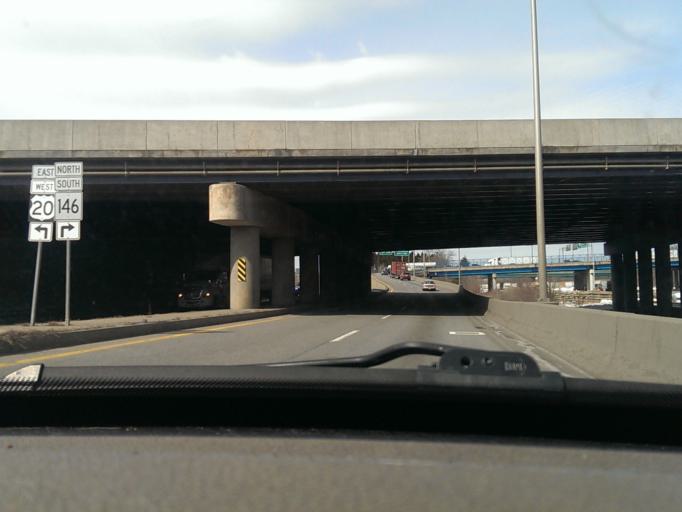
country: US
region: Massachusetts
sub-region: Worcester County
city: Millbury
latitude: 42.2084
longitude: -71.7833
